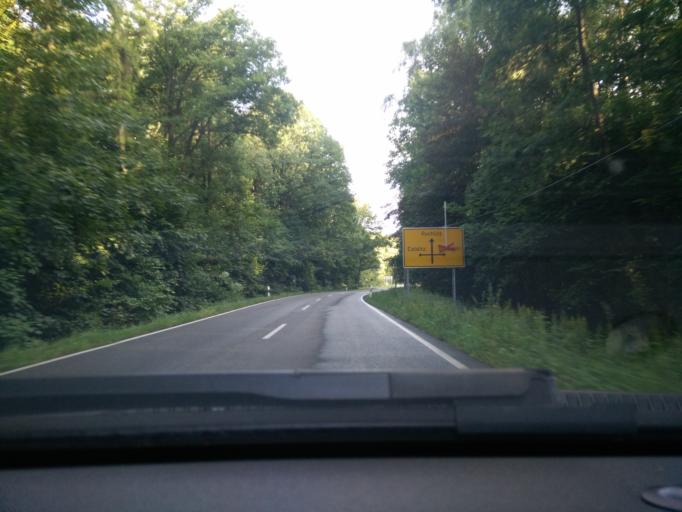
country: DE
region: Saxony
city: Konigsfeld
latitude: 51.0771
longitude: 12.7221
